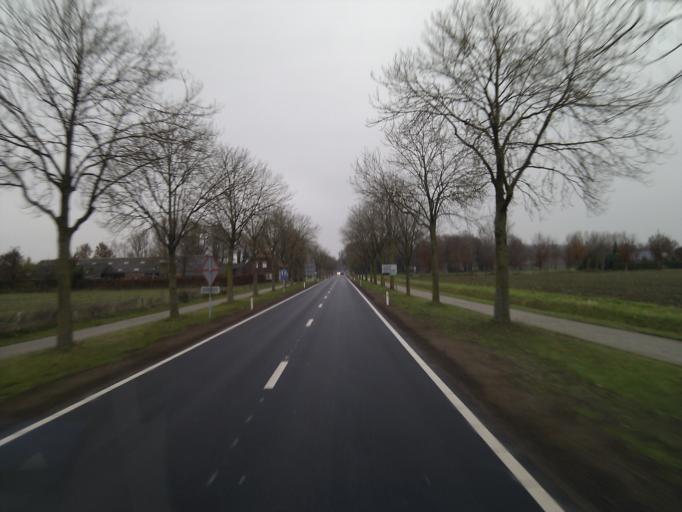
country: NL
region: North Brabant
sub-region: Gemeente Sint-Oedenrode
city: Sint-Oedenrode
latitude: 51.5785
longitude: 5.4614
